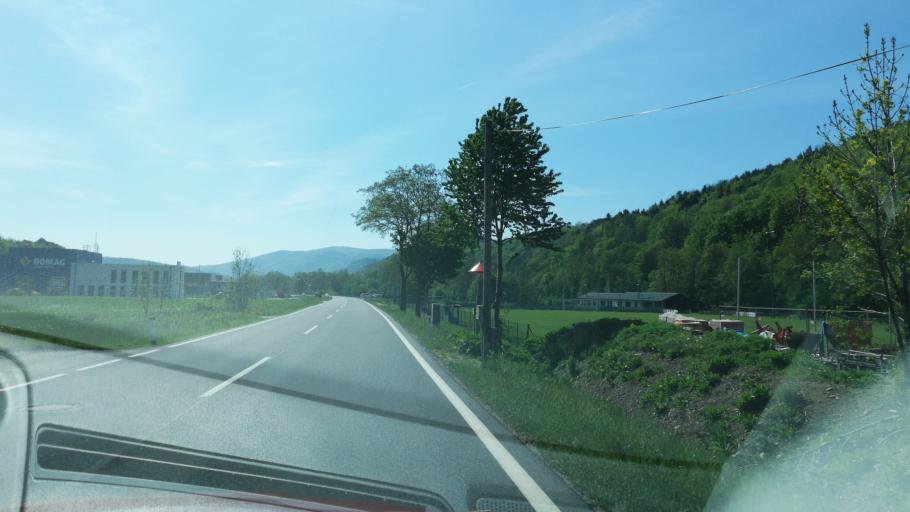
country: AT
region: Lower Austria
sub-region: Politischer Bezirk Baden
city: Alland
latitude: 48.0651
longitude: 16.0661
